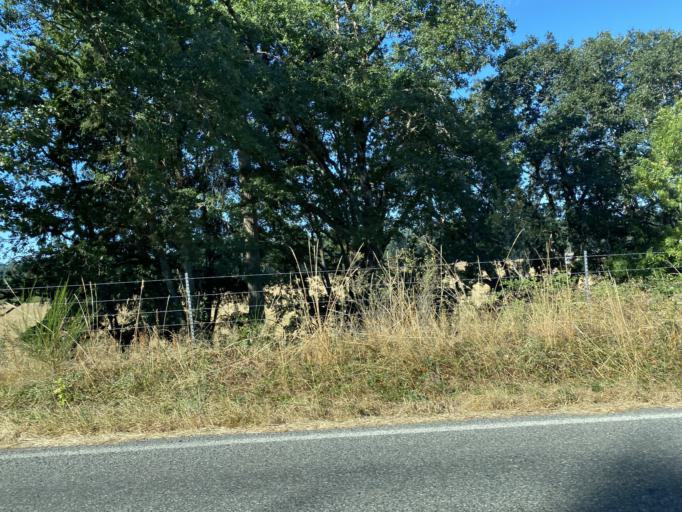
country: US
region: Washington
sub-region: Thurston County
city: Rainier
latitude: 46.8949
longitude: -122.7539
